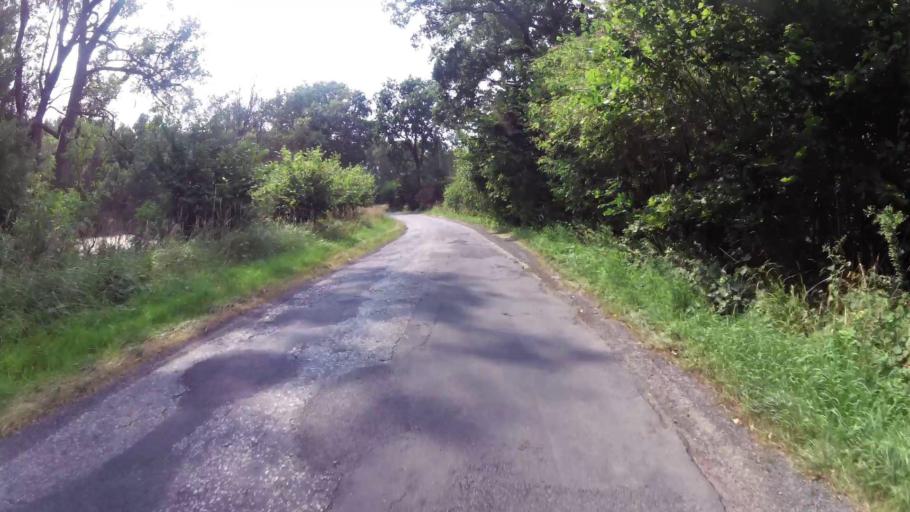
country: PL
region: West Pomeranian Voivodeship
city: Trzcinsko Zdroj
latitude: 52.9040
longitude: 14.5346
